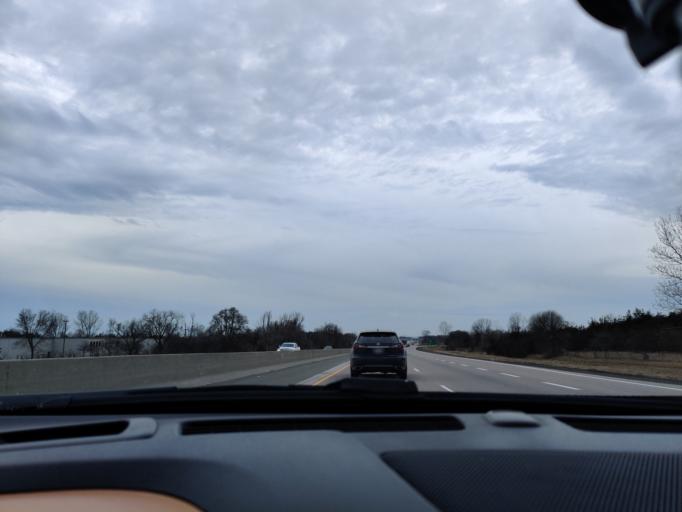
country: CA
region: Ontario
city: Belleville
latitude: 44.1965
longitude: -77.3821
